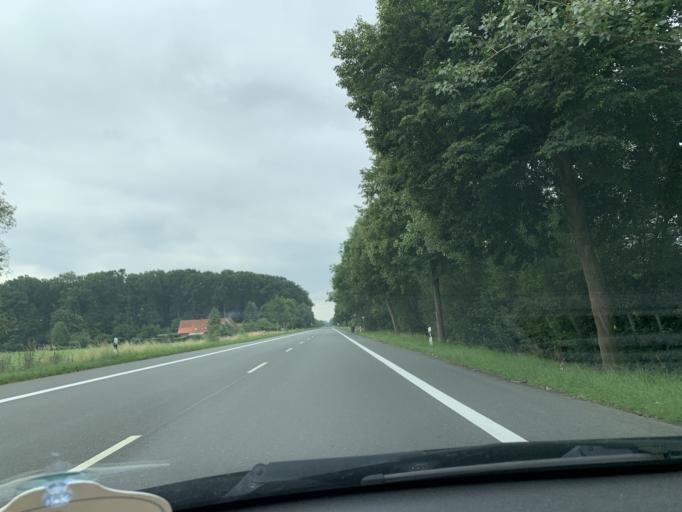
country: DE
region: North Rhine-Westphalia
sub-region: Regierungsbezirk Munster
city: Warendorf
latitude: 51.9168
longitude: 8.0401
